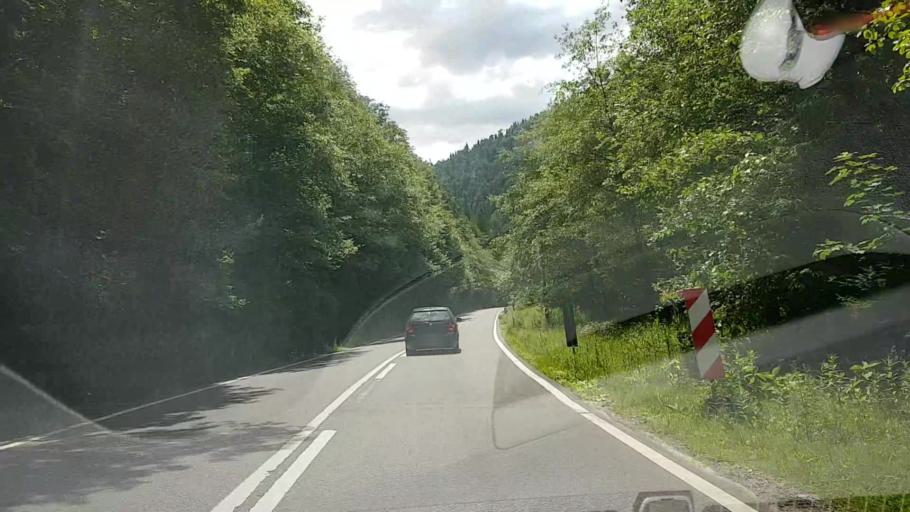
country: RO
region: Suceava
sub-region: Comuna Brosteni
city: Brosteni
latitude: 47.2798
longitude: 25.6502
